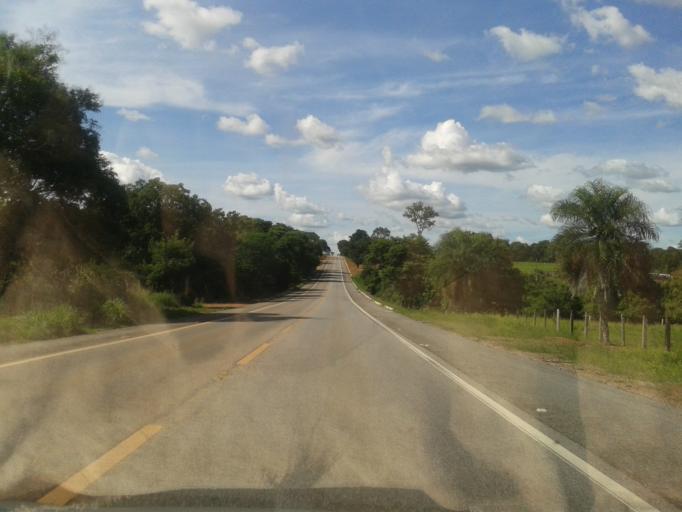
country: BR
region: Goias
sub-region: Mozarlandia
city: Mozarlandia
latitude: -15.1171
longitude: -50.6052
